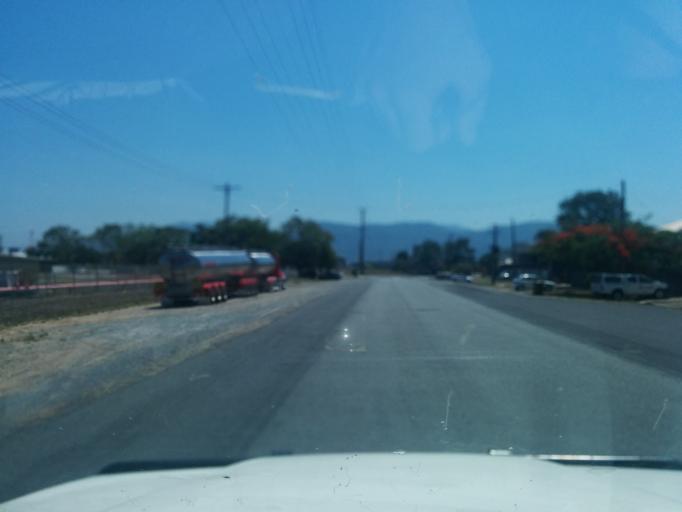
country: AU
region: Queensland
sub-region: Cairns
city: Cairns
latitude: -16.9299
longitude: 145.7737
